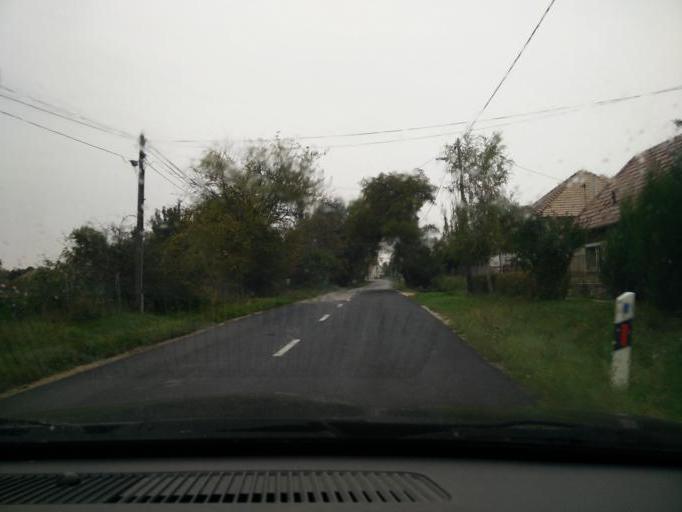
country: HU
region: Pest
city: Perbal
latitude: 47.6246
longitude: 18.7776
